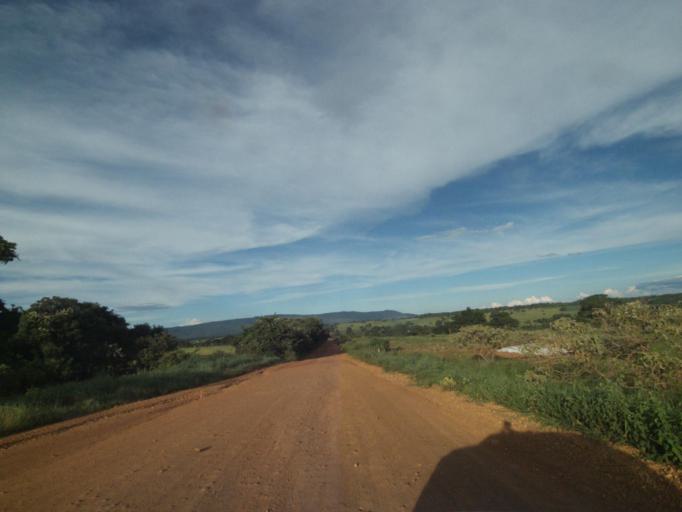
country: BR
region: Goias
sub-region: Jaragua
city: Jaragua
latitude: -15.8650
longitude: -49.4006
